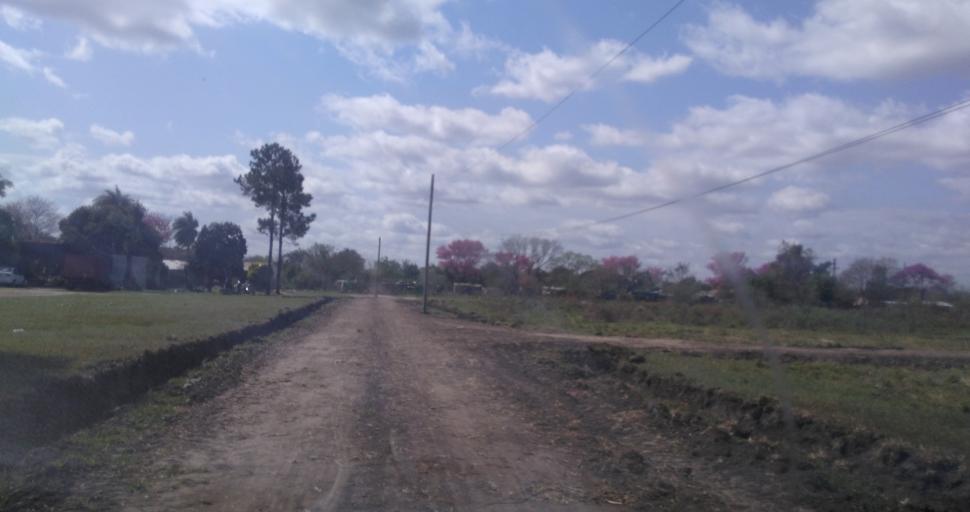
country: AR
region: Chaco
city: Fontana
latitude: -27.4291
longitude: -59.0230
